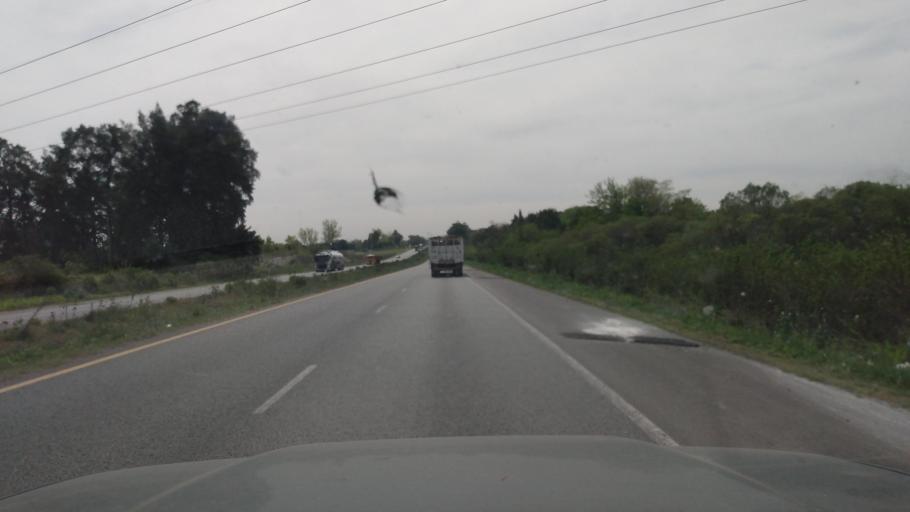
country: AR
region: Buenos Aires
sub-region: Partido de Lujan
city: Lujan
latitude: -34.4526
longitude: -59.0552
